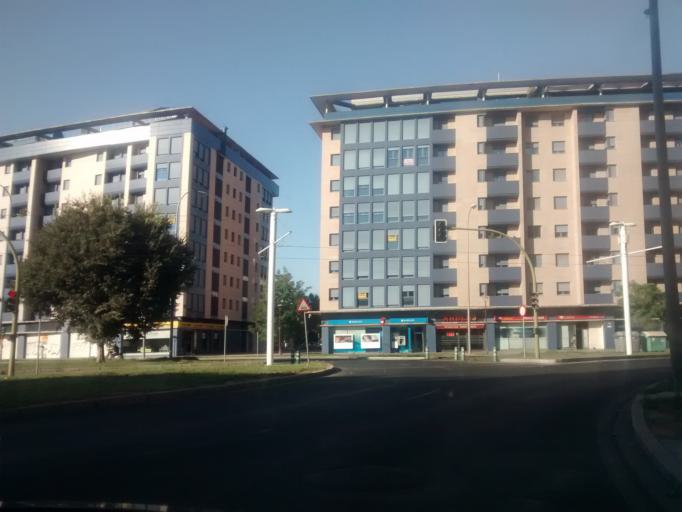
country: ES
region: Andalusia
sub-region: Provincia de Sevilla
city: Sevilla
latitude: 37.3795
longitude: -5.9831
